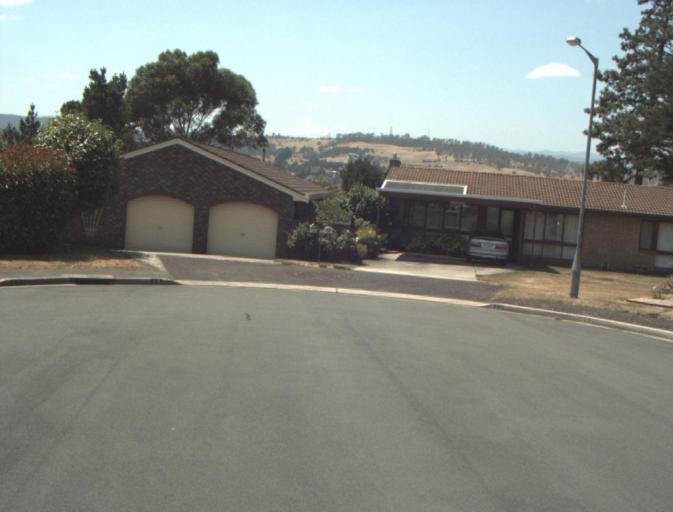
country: AU
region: Tasmania
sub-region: Launceston
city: Newstead
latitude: -41.4676
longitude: 147.1835
